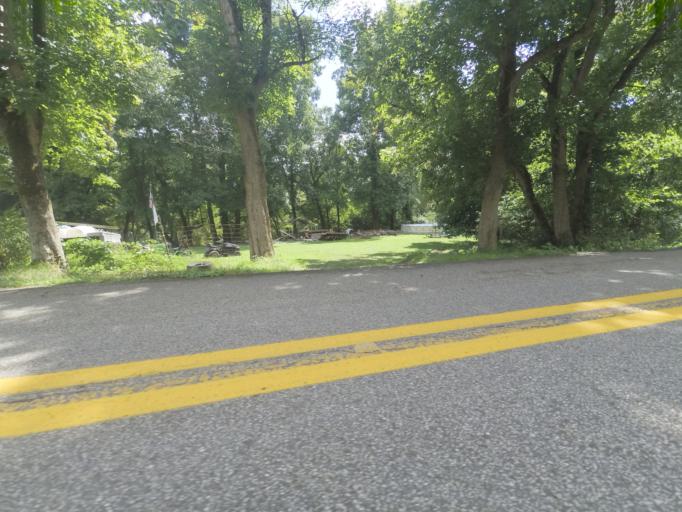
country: US
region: West Virginia
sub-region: Cabell County
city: Pea Ridge
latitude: 38.4282
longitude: -82.3054
